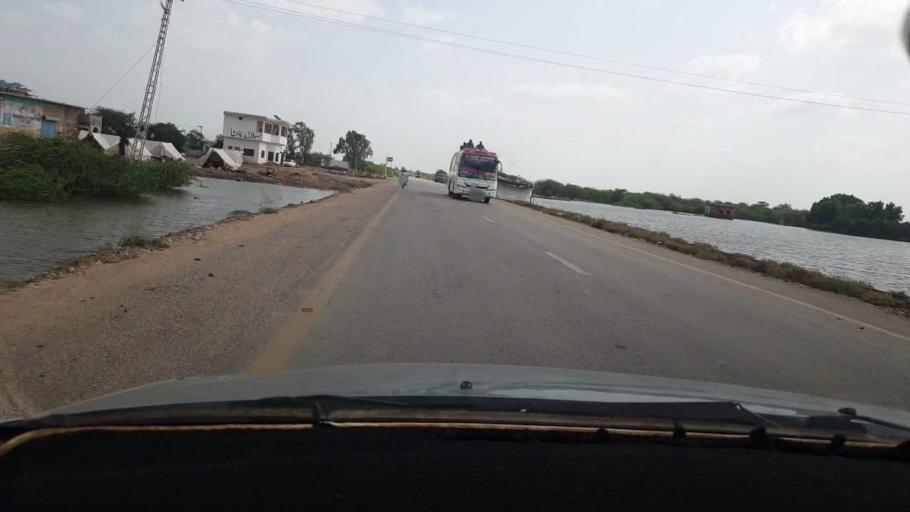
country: PK
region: Sindh
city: Naukot
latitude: 24.9884
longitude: 69.2922
